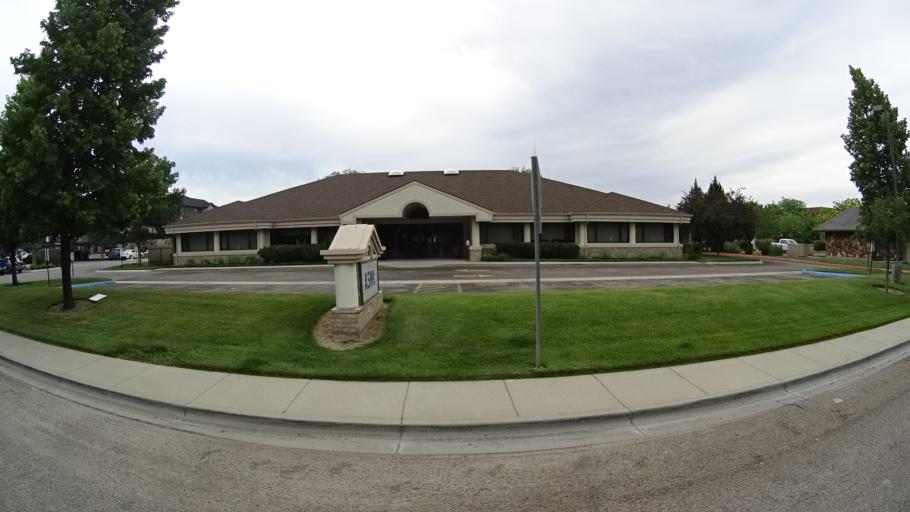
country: US
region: Idaho
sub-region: Ada County
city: Boise
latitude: 43.5744
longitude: -116.2236
